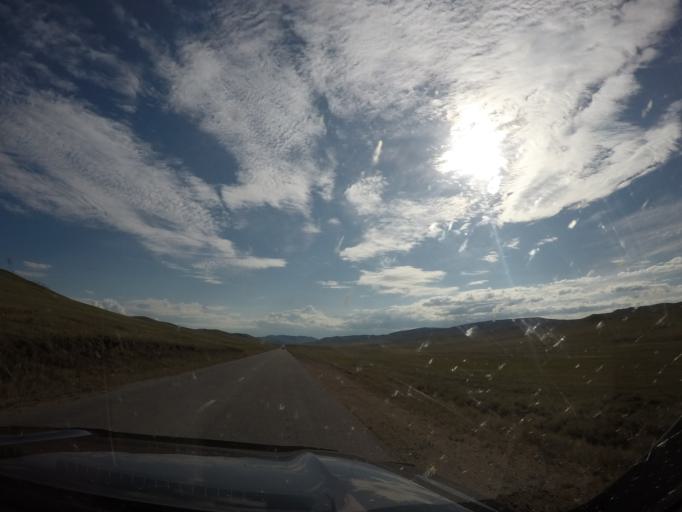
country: MN
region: Hentiy
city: Modot
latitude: 47.7485
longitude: 108.6170
